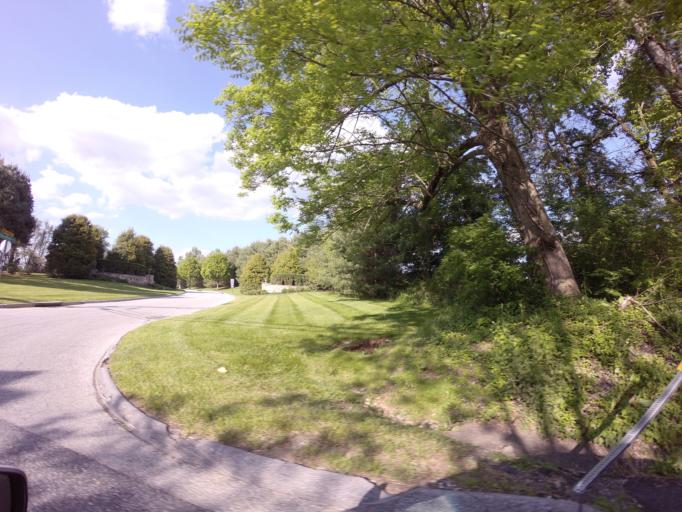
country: US
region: Maryland
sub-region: Baltimore County
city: Hunt Valley
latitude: 39.5099
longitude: -76.7026
